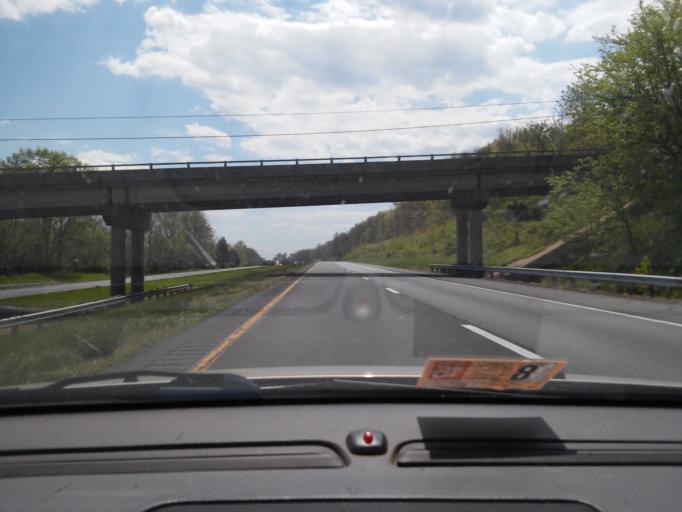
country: US
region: West Virginia
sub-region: Berkeley County
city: Inwood
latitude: 39.3152
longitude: -78.0757
